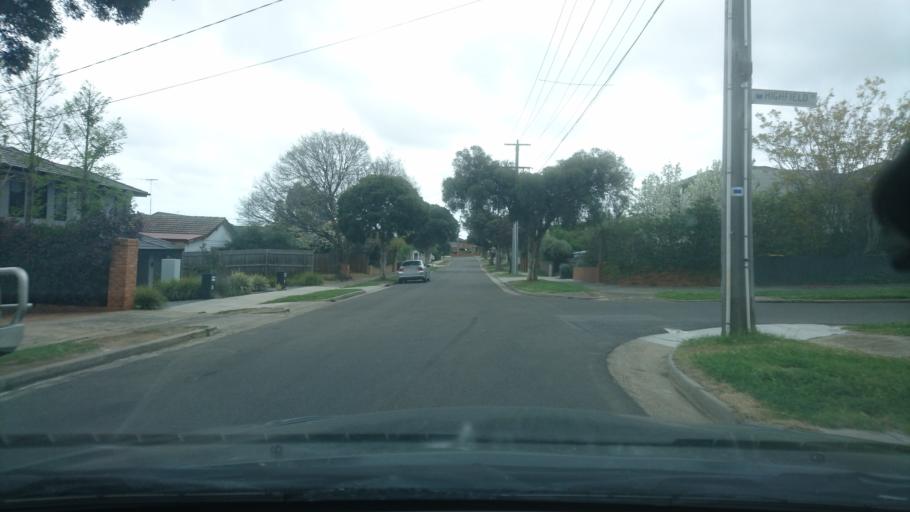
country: AU
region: Victoria
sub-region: Monash
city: Chadstone
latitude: -37.8888
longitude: 145.1047
